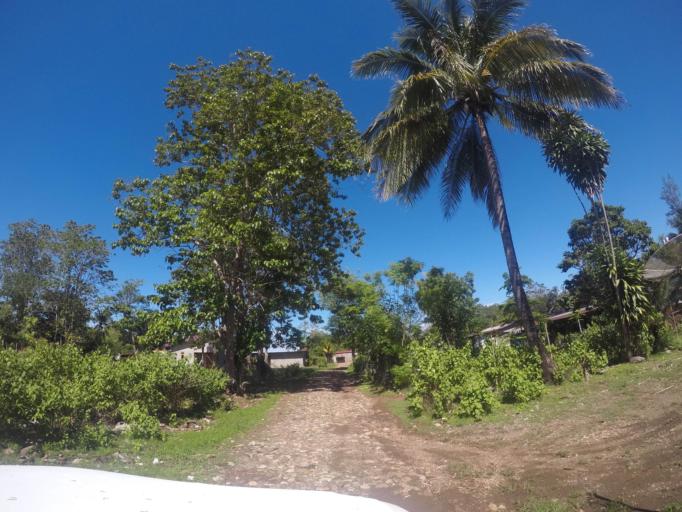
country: TL
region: Bobonaro
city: Maliana
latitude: -8.9888
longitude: 125.1999
